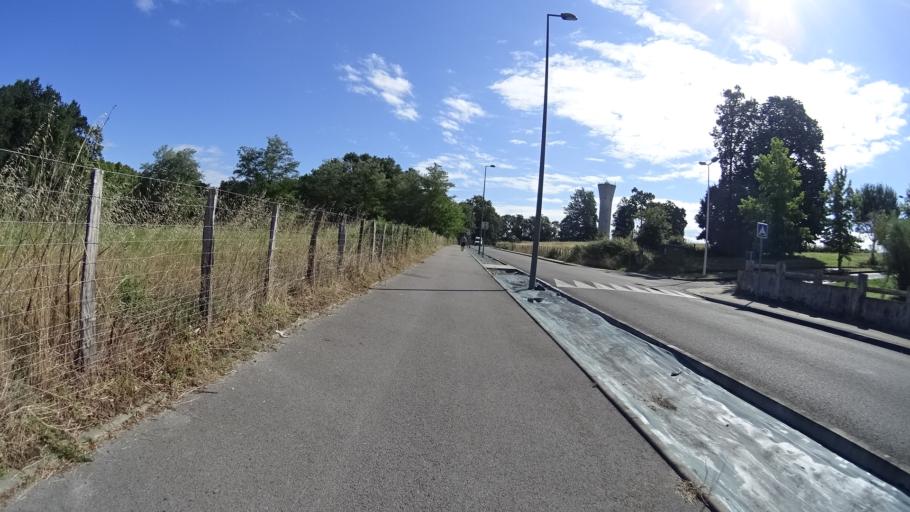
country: FR
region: Aquitaine
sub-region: Departement des Landes
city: Dax
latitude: 43.6967
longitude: -1.0772
